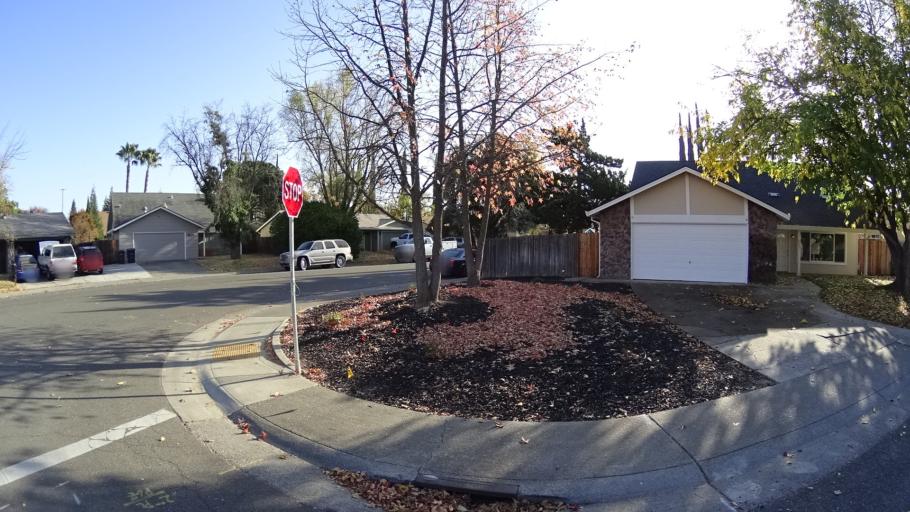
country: US
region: California
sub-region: Sacramento County
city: Citrus Heights
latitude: 38.6979
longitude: -121.2654
